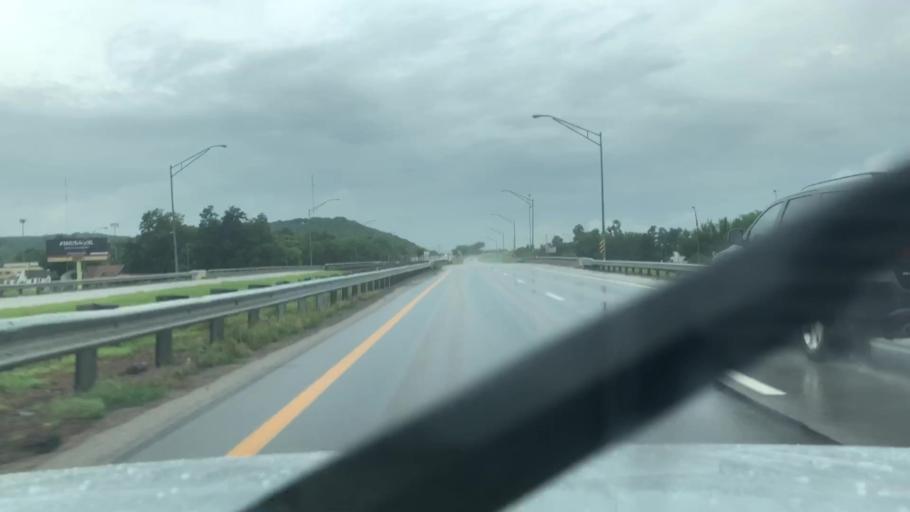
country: US
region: Oklahoma
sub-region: Tulsa County
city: Tulsa
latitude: 36.1036
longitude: -96.0089
